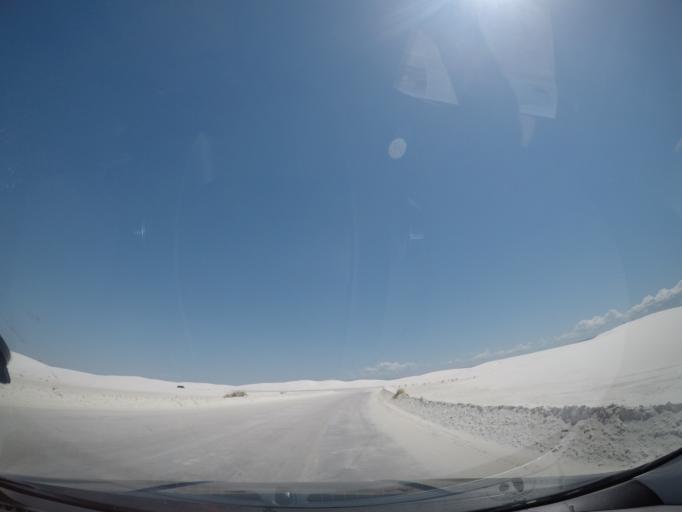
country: US
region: New Mexico
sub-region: Otero County
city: Holloman Air Force Base
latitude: 32.8159
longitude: -106.2638
